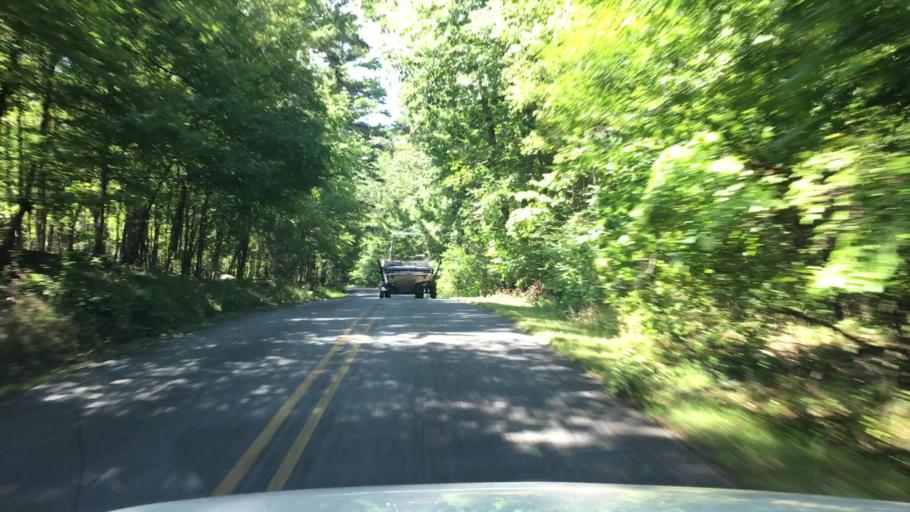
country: US
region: Arkansas
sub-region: Garland County
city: Piney
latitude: 34.5378
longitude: -93.3413
